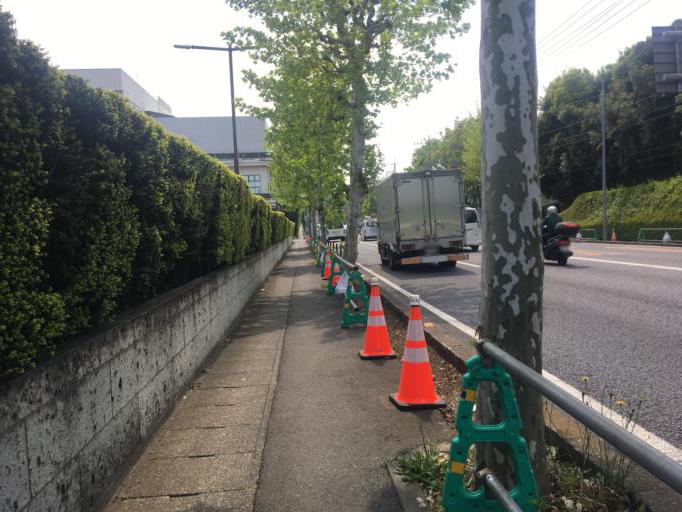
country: JP
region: Saitama
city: Wako
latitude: 35.7813
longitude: 139.6140
